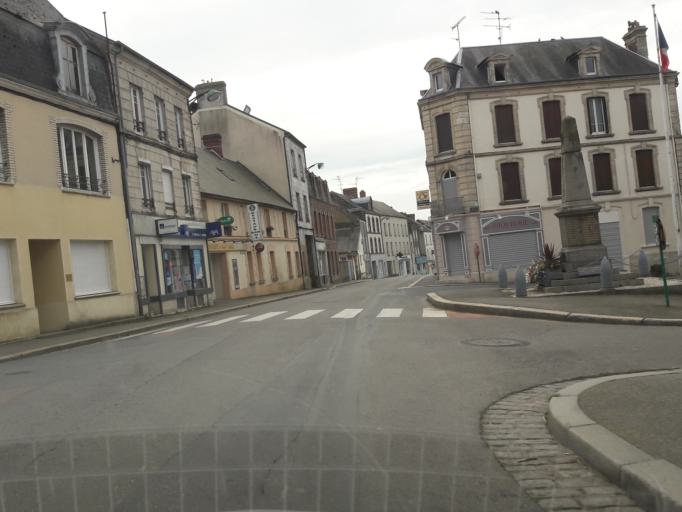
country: FR
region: Lower Normandy
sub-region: Departement du Calvados
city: Cahagnes
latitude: 49.0906
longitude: -0.8059
